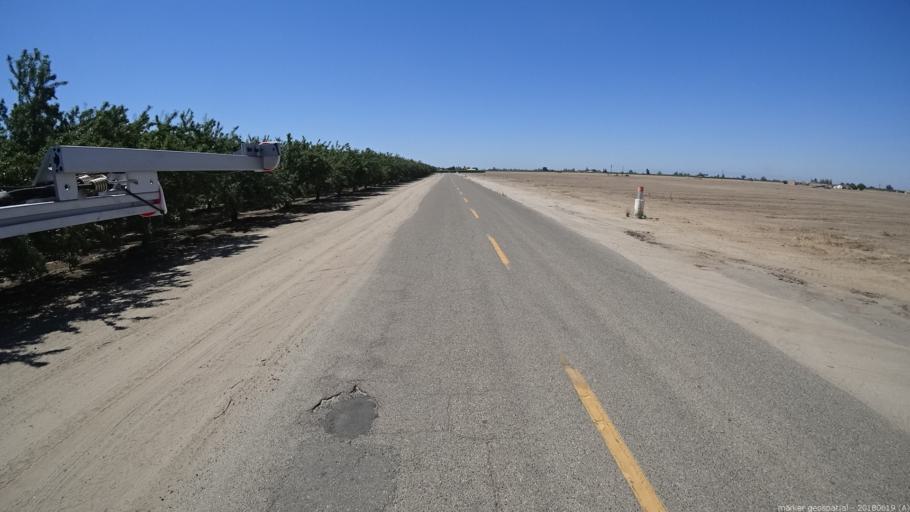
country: US
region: California
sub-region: Fresno County
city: Biola
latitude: 36.8396
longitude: -120.0649
